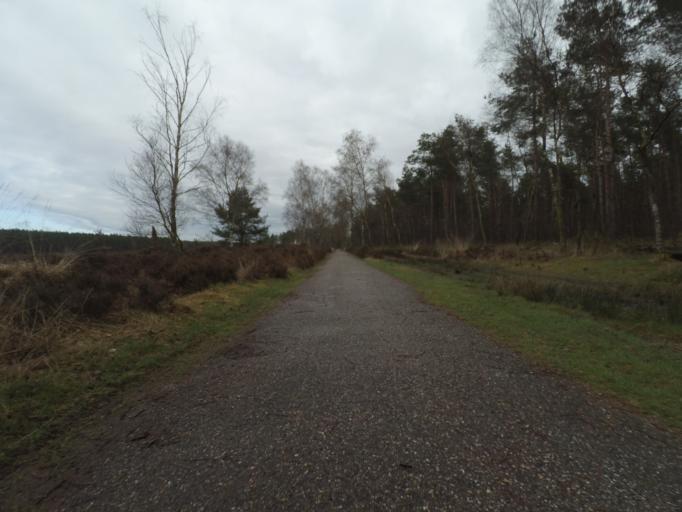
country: NL
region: Gelderland
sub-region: Gemeente Arnhem
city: Gulden Bodem
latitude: 52.0299
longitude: 5.9099
